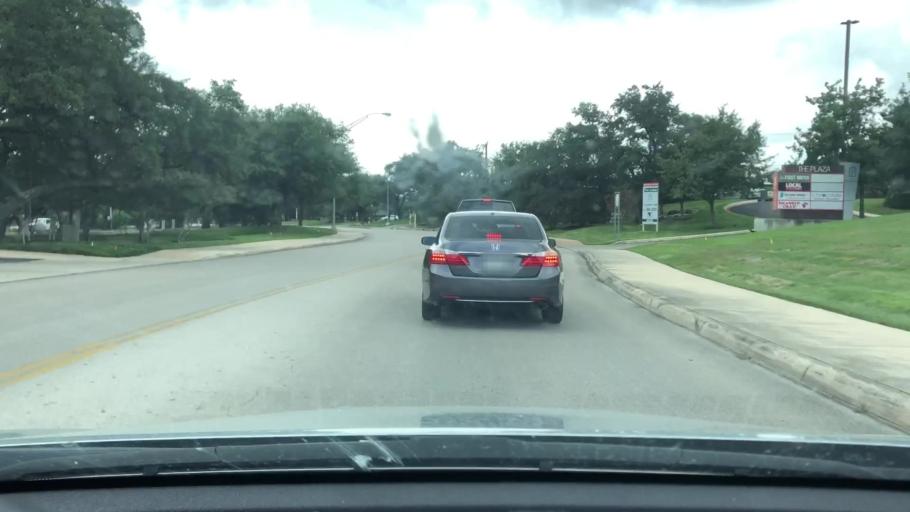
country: US
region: Texas
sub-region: Bexar County
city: Hollywood Park
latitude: 29.6143
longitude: -98.4834
